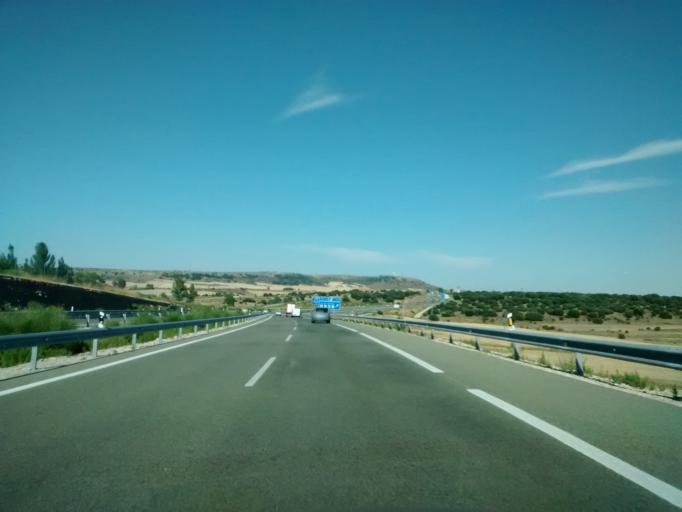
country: ES
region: Castille-La Mancha
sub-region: Provincia de Guadalajara
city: Sauca
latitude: 41.0301
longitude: -2.5005
